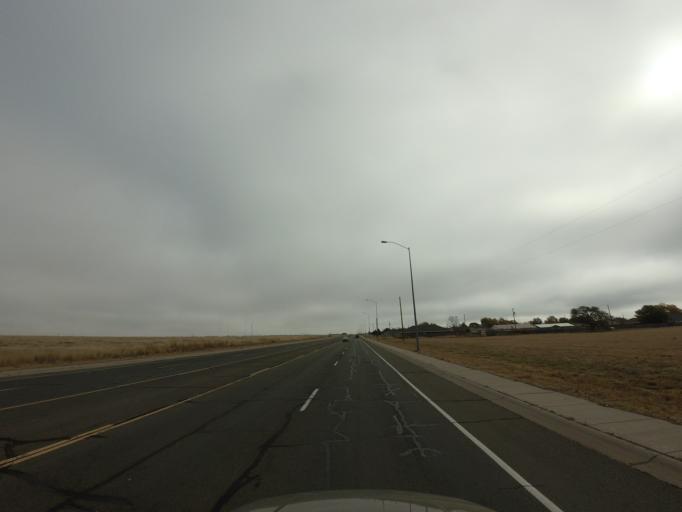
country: US
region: New Mexico
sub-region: Curry County
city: Clovis
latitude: 34.4340
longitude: -103.2290
